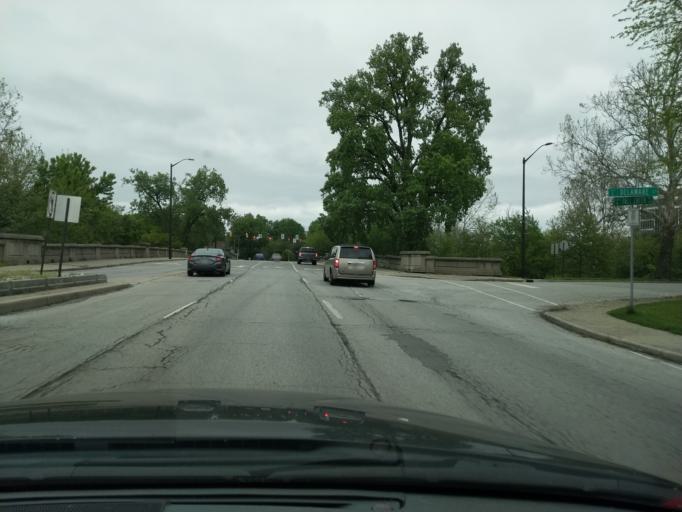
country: US
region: Indiana
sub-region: Marion County
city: Indianapolis
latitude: 39.8048
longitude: -86.1531
